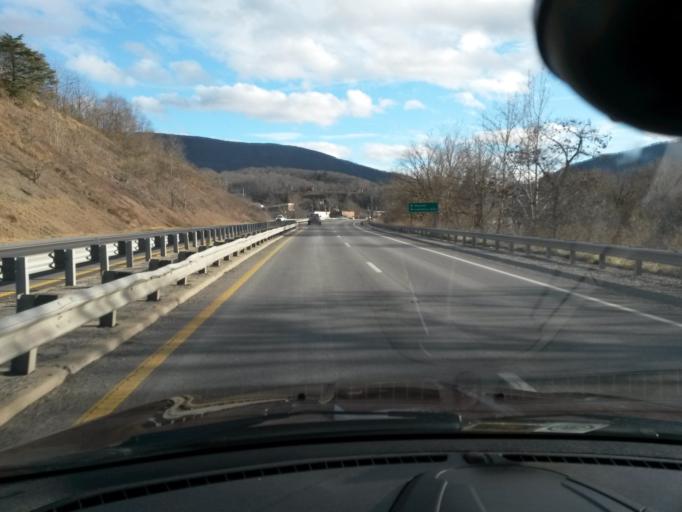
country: US
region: Virginia
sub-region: Giles County
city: Narrows
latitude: 37.3849
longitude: -80.8262
